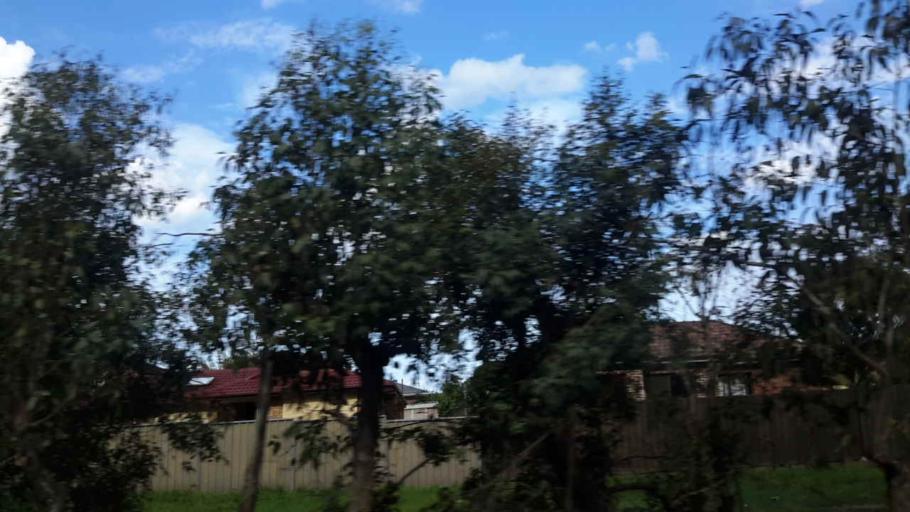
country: AU
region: New South Wales
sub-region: Penrith Municipality
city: Werrington Downs
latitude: -33.7340
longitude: 150.7179
